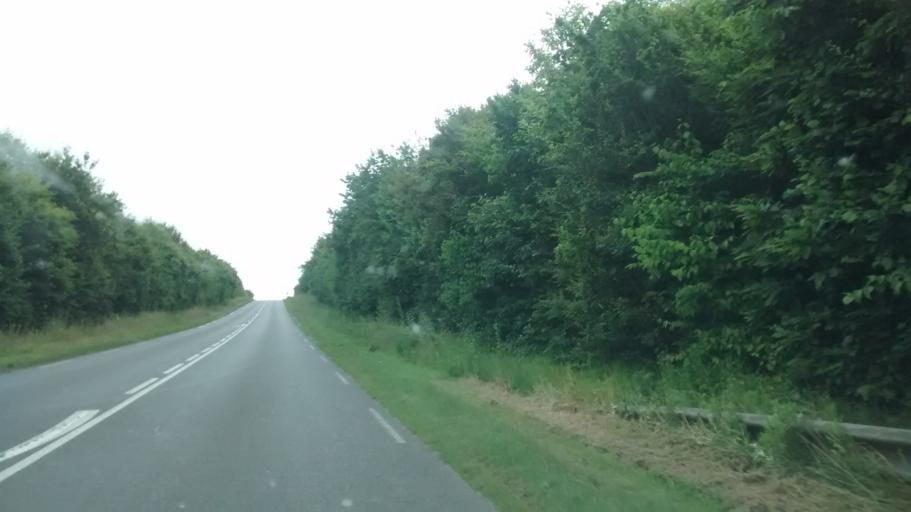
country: FR
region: Brittany
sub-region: Departement d'Ille-et-Vilaine
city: Saint-Jouan-des-Guerets
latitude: 48.6287
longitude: -1.9770
